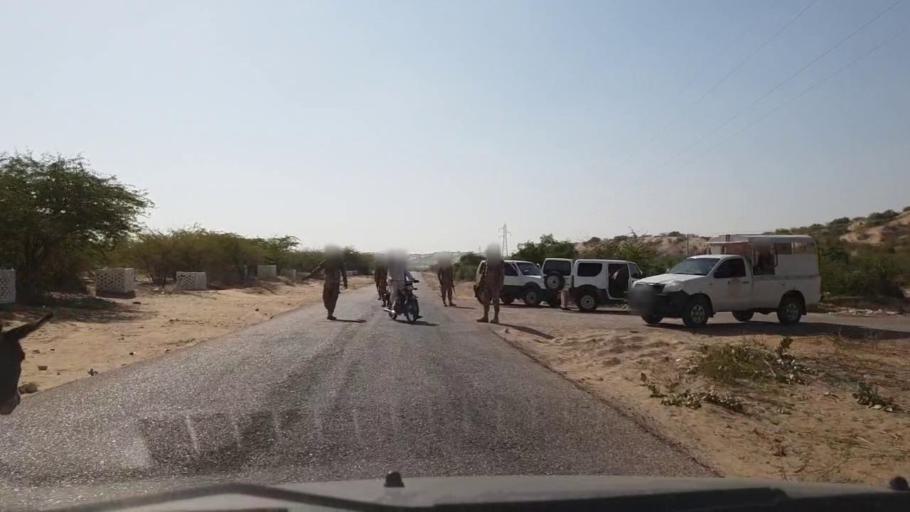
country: PK
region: Sindh
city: Diplo
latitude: 24.4872
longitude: 69.5882
